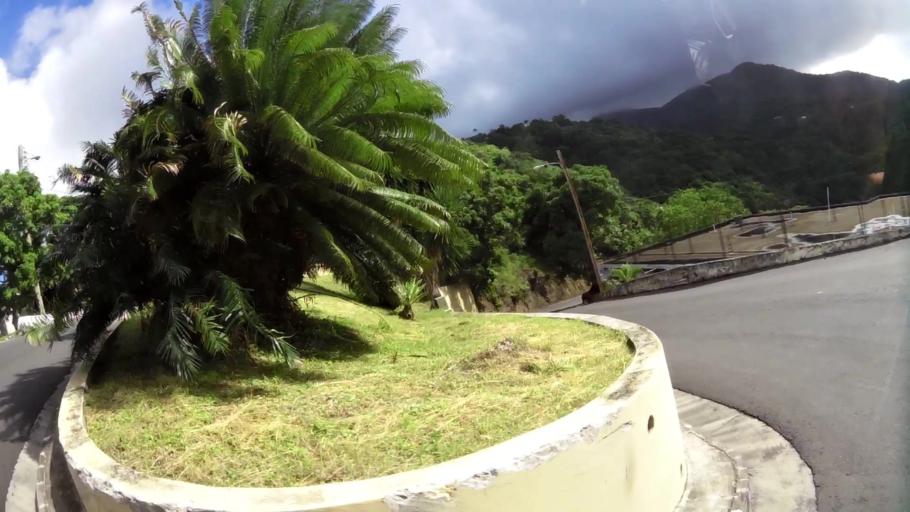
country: MS
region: Saint Peter
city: Saint Peters
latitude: 16.7802
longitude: -62.2083
